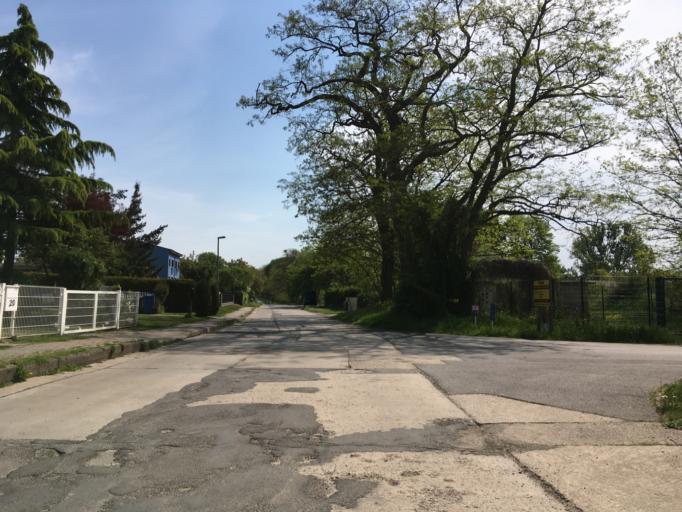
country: DE
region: Brandenburg
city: Werneuchen
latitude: 52.6003
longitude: 13.7455
